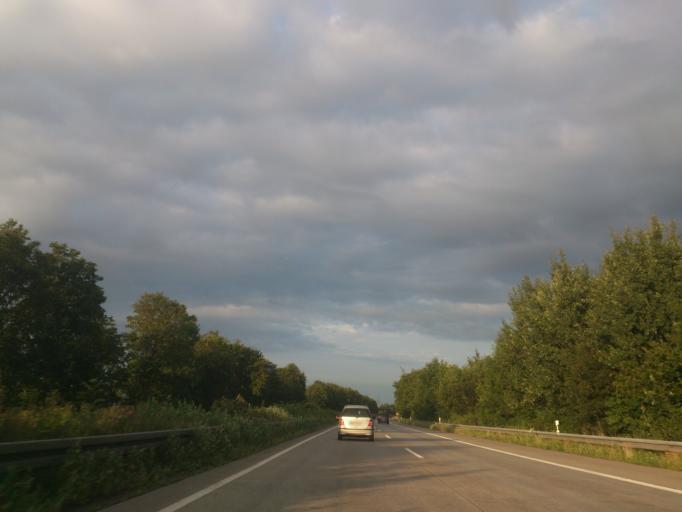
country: DE
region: North Rhine-Westphalia
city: Wickede
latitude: 51.5334
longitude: 7.8326
